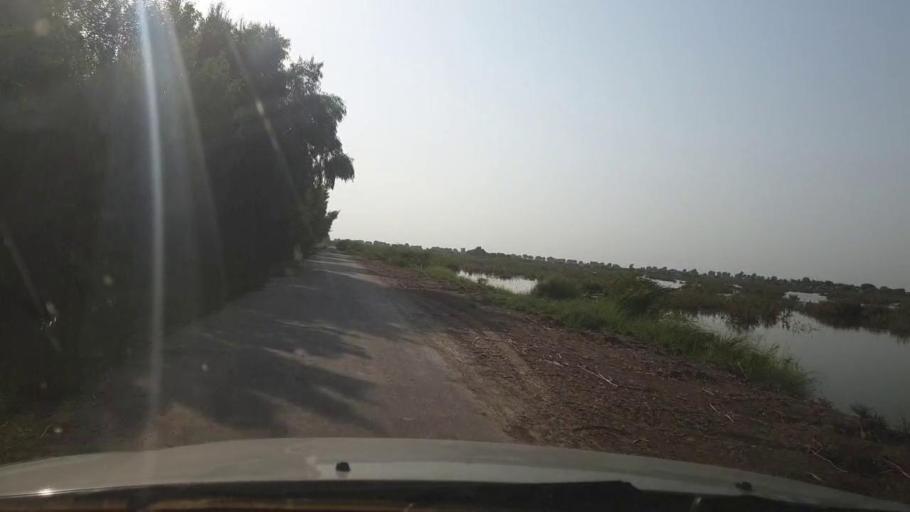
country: PK
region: Sindh
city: Tando Ghulam Ali
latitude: 25.1893
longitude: 68.9385
